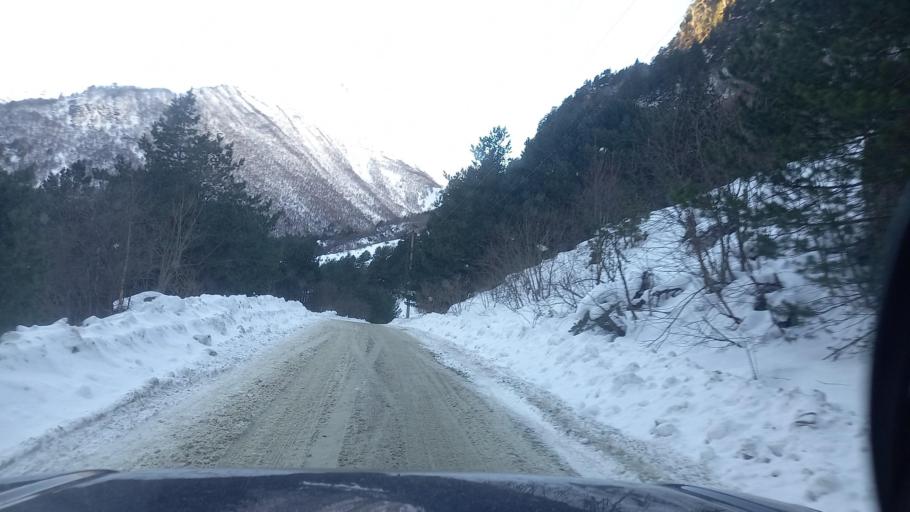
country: RU
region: Kabardino-Balkariya
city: Verkhnyaya Balkariya
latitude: 42.9024
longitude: 43.5912
